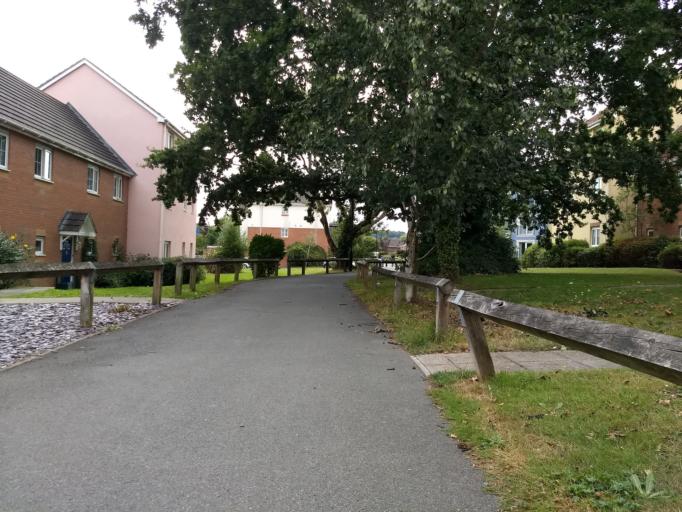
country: GB
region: England
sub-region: Isle of Wight
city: Newport
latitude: 50.7005
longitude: -1.3042
